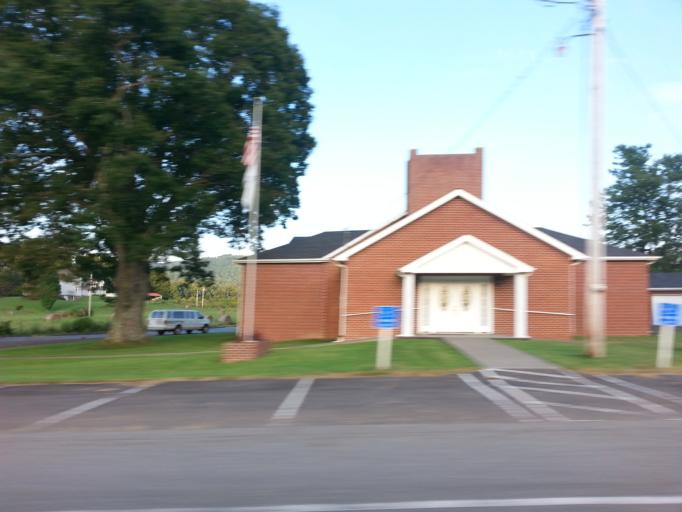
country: US
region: Tennessee
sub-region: Johnson County
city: Mountain City
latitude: 36.5031
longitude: -81.9395
